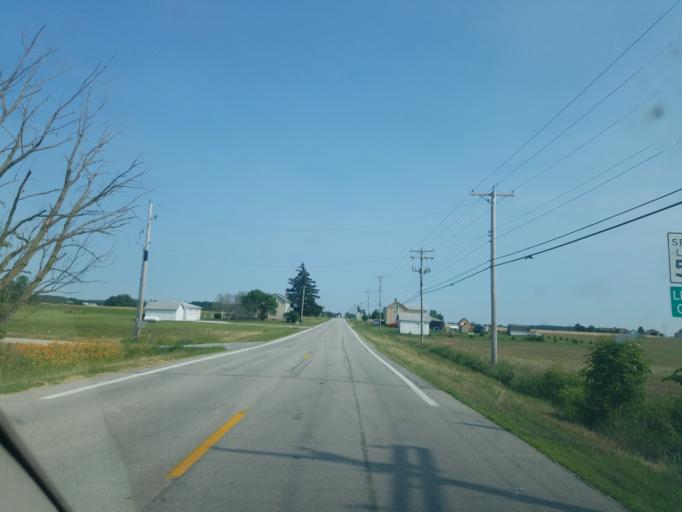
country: US
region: Ohio
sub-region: Wyandot County
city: Carey
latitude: 41.0480
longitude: -83.3152
